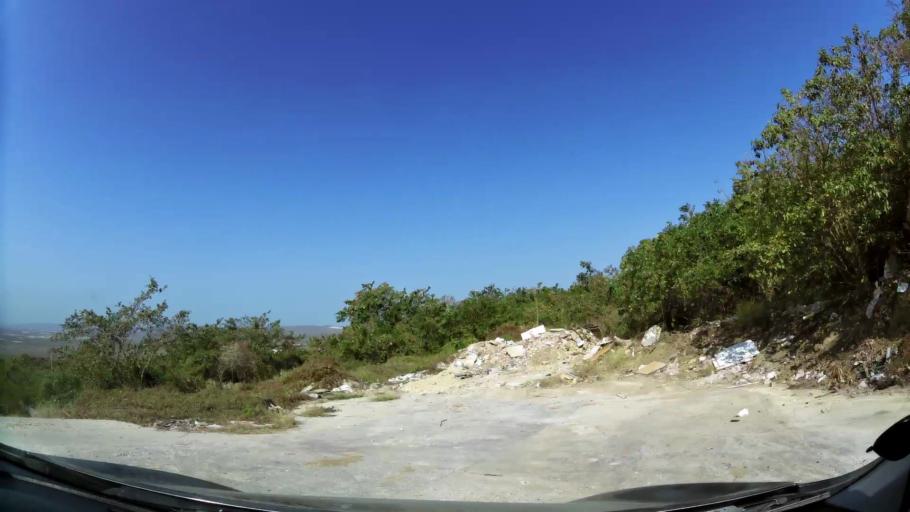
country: CO
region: Atlantico
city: Barranquilla
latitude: 10.9926
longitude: -74.8303
